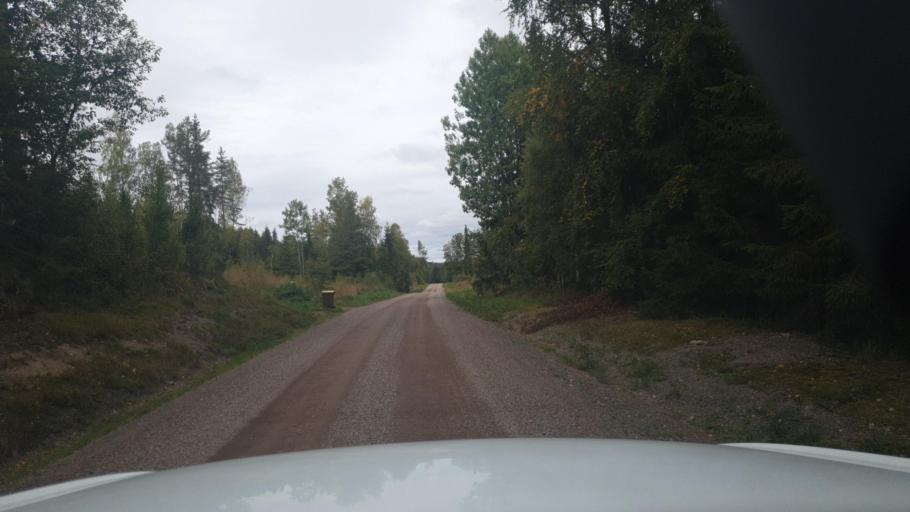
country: SE
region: Vaermland
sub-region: Eda Kommun
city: Charlottenberg
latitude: 60.0769
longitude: 12.5258
